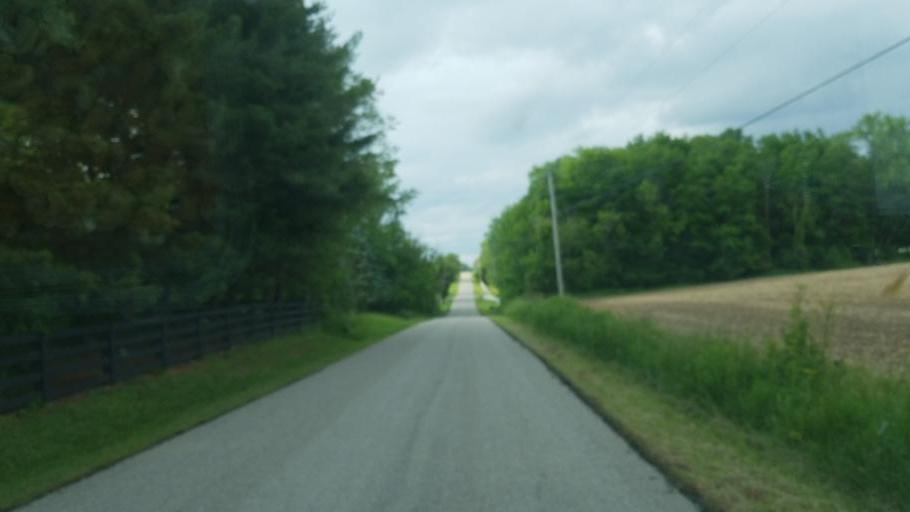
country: US
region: Ohio
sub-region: Knox County
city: Centerburg
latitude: 40.3277
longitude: -82.7764
